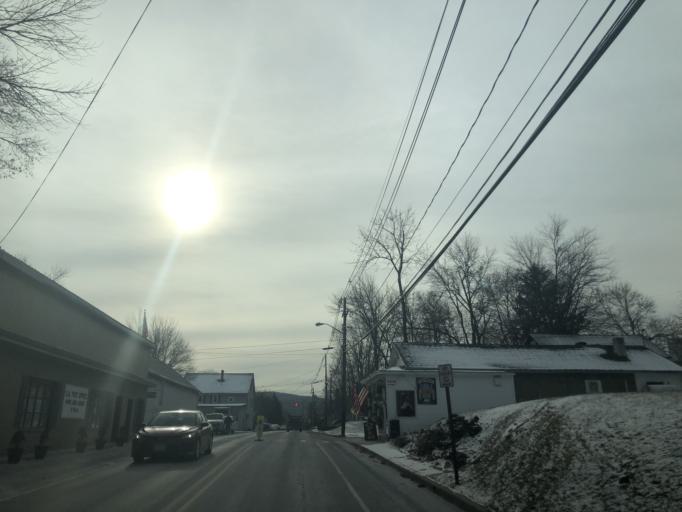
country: US
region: New Jersey
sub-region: Warren County
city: Oxford
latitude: 40.9120
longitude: -74.9681
